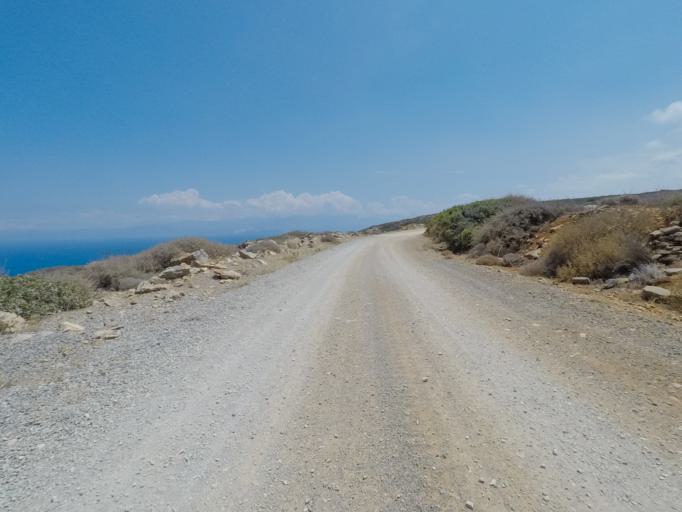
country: GR
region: Crete
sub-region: Nomos Lasithiou
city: Elounda
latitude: 35.3239
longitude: 25.7551
